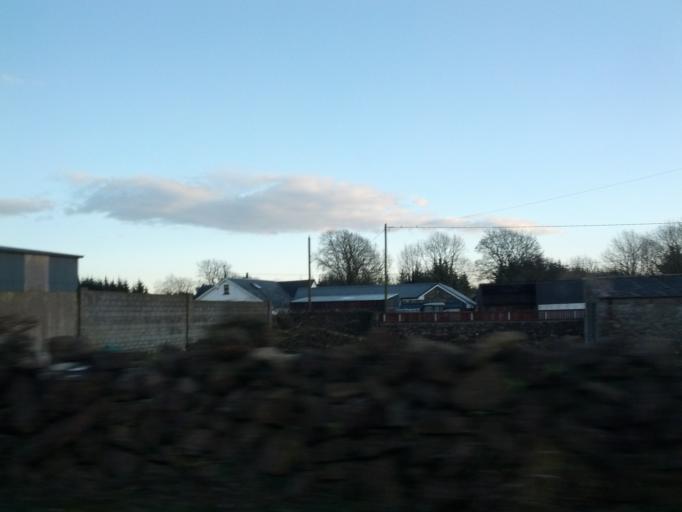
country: IE
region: Connaught
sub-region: County Galway
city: Athenry
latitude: 53.3271
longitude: -8.6574
